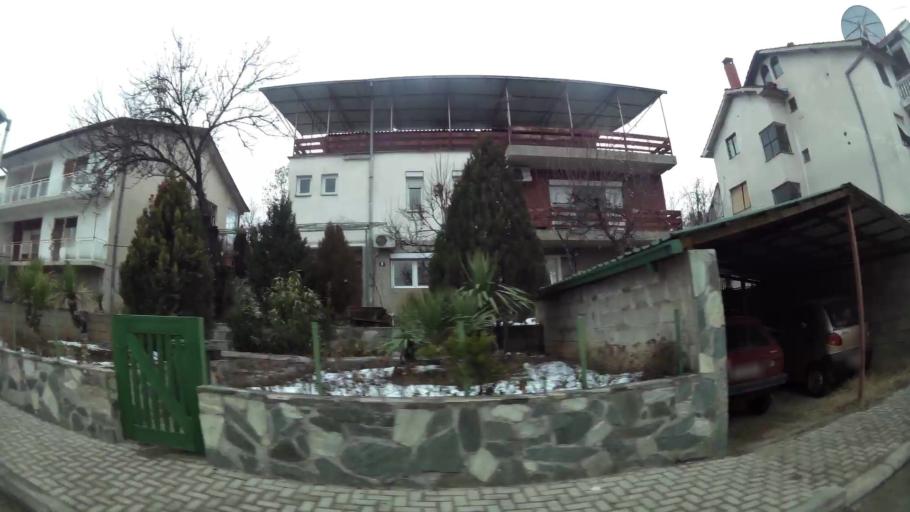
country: MK
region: Cair
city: Cair
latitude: 42.0139
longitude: 21.4559
